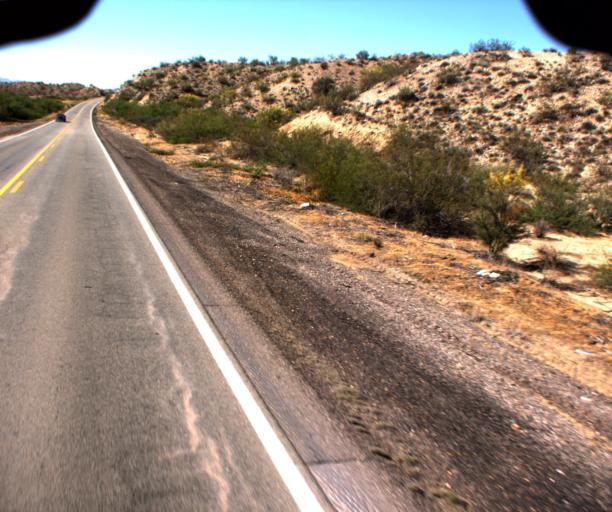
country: US
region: Arizona
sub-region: Yavapai County
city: Bagdad
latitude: 34.7850
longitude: -113.6236
